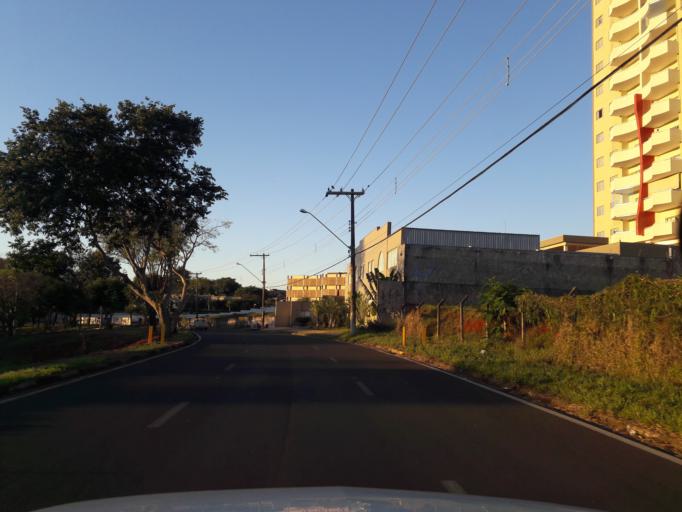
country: BR
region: Sao Paulo
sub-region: Moji-Guacu
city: Mogi-Gaucu
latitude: -22.3650
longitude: -46.9339
